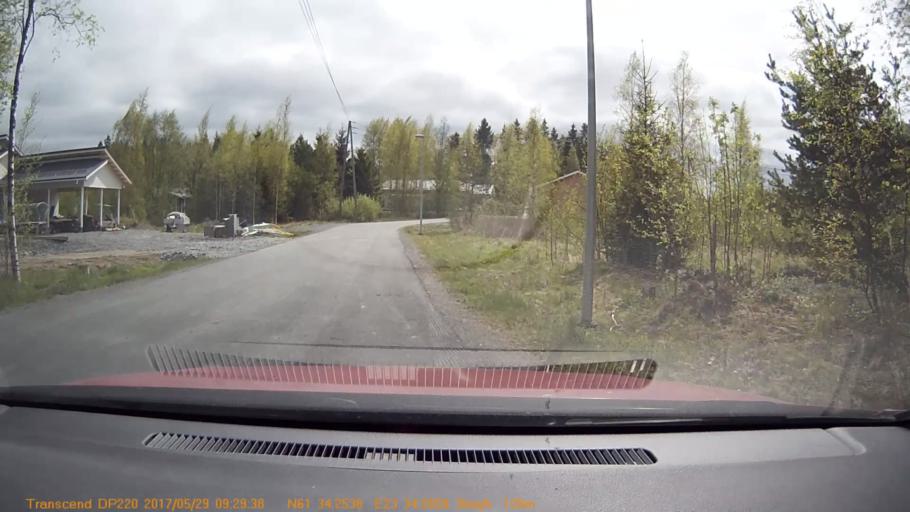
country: FI
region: Pirkanmaa
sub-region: Tampere
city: Yloejaervi
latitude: 61.5708
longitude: 23.5713
